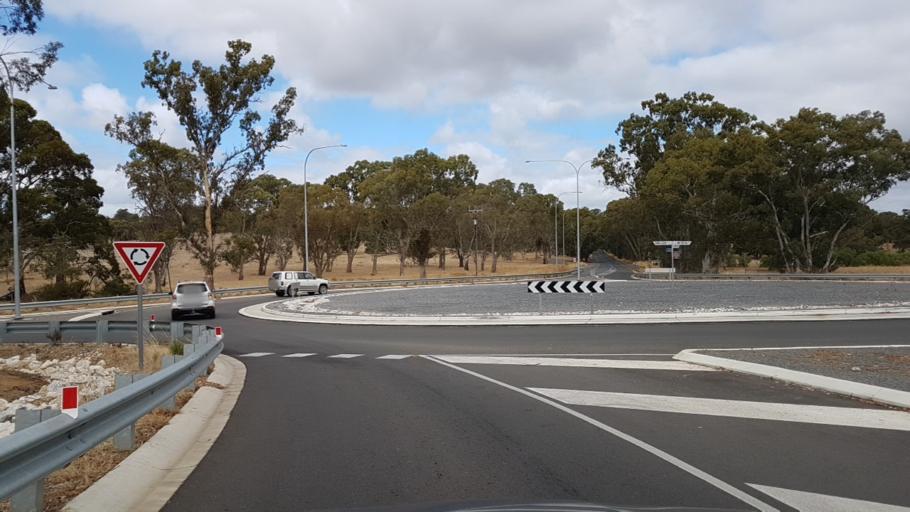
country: AU
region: South Australia
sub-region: Playford
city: One Tree Hill
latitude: -34.7145
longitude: 138.7839
